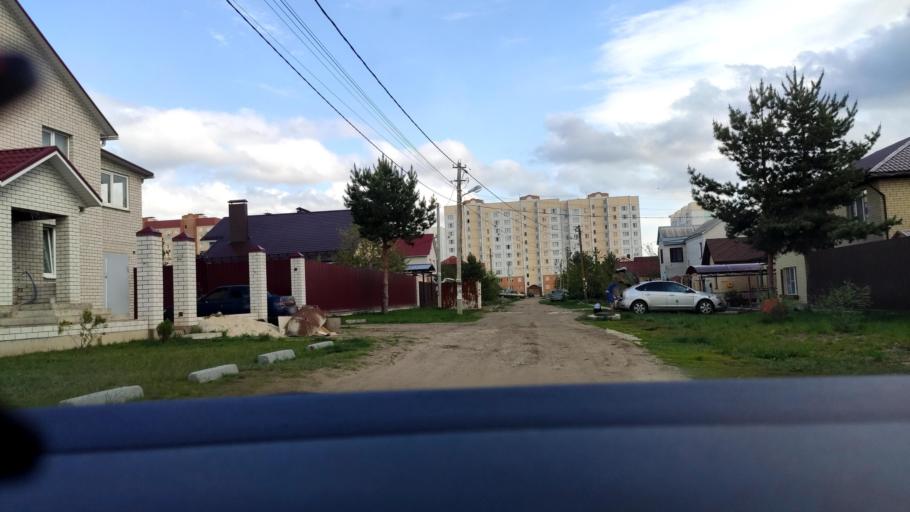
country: RU
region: Voronezj
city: Shilovo
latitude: 51.5647
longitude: 39.1113
